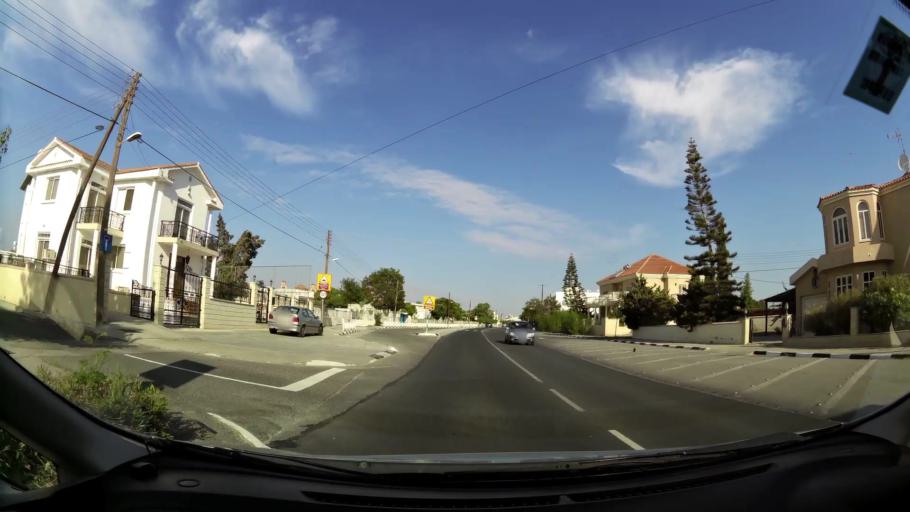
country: CY
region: Larnaka
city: Aradippou
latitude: 34.9430
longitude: 33.5982
